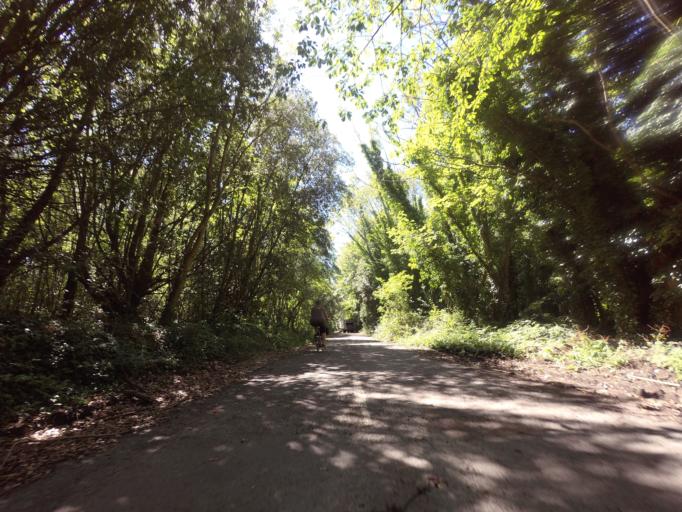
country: GB
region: England
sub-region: Kent
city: Eastry
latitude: 51.2201
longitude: 1.3002
